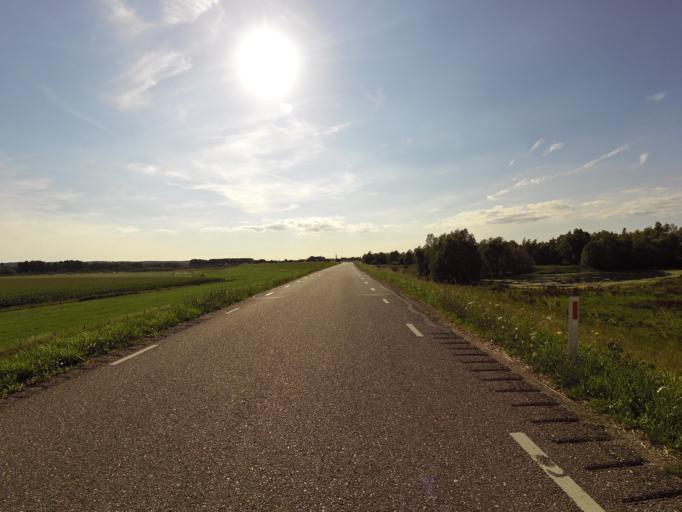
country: DE
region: North Rhine-Westphalia
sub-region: Regierungsbezirk Dusseldorf
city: Kranenburg
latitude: 51.8492
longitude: 5.9848
